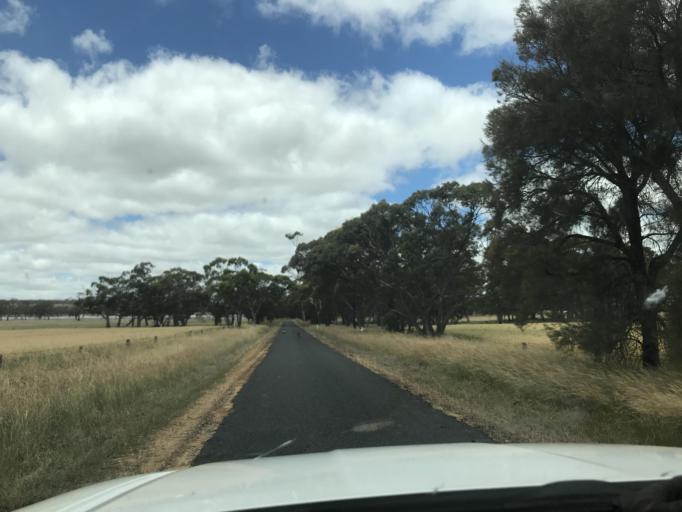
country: AU
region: South Australia
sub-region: Tatiara
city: Bordertown
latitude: -36.3623
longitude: 141.4011
